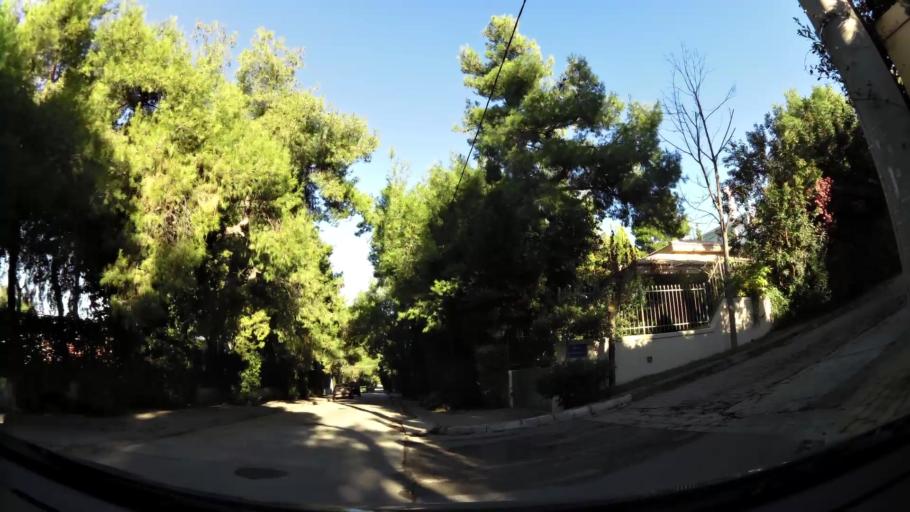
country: GR
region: Attica
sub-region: Nomarchia Athinas
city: Ekali
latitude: 38.1102
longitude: 23.8501
